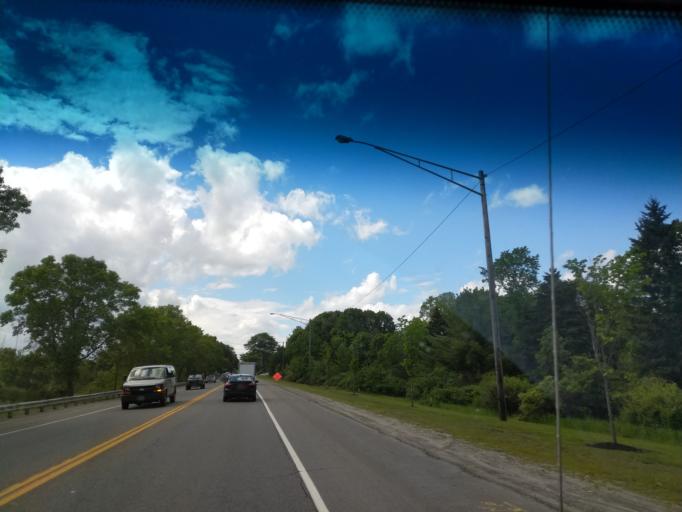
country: US
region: Maine
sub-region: Cumberland County
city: Westbrook
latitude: 43.6799
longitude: -70.3757
